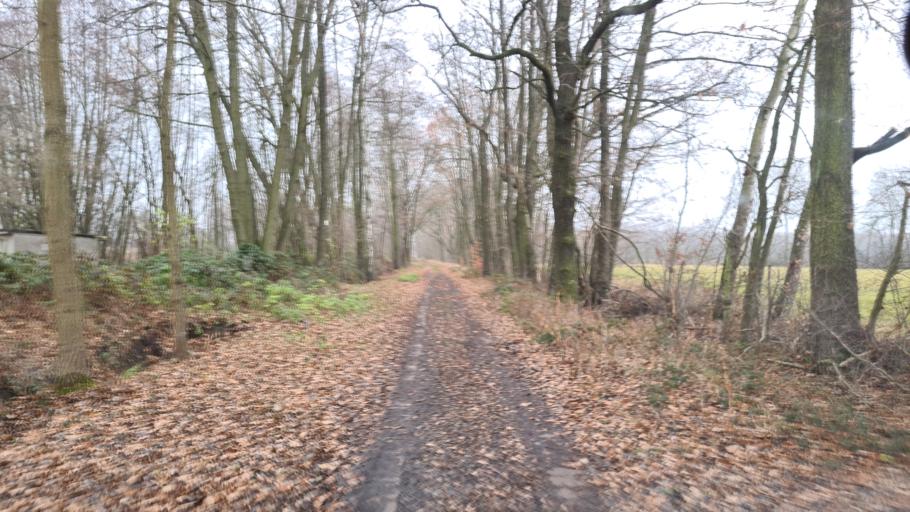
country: DE
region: Brandenburg
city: Doberlug-Kirchhain
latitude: 51.6268
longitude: 13.5313
